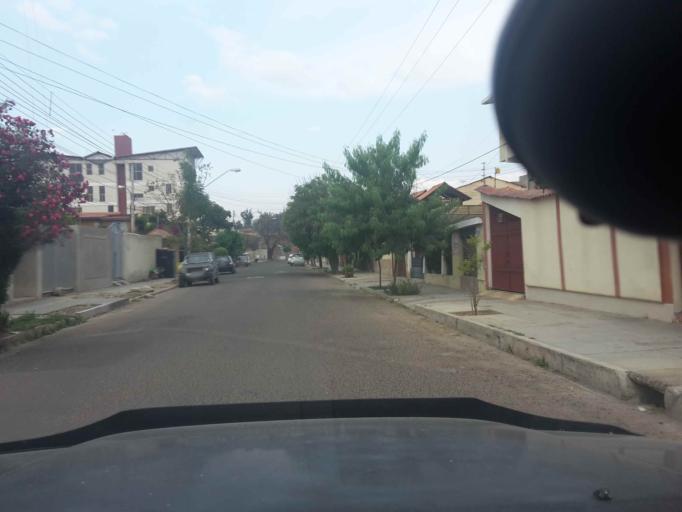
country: BO
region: Cochabamba
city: Cochabamba
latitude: -17.3788
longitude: -66.1679
